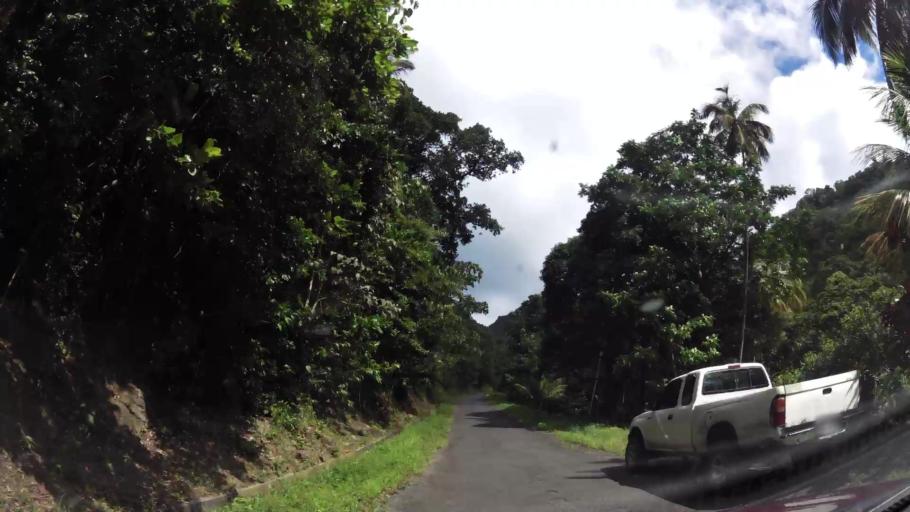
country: DM
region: Saint John
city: Portsmouth
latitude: 15.6087
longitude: -61.4543
